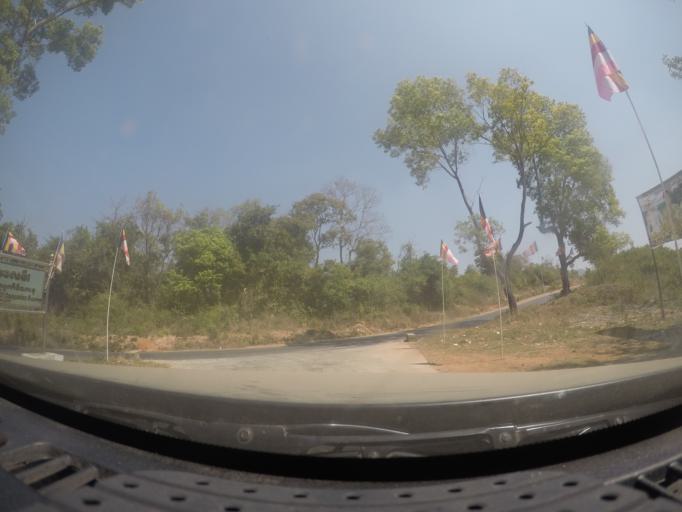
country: MM
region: Shan
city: Taunggyi
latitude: 20.9171
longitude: 96.5635
